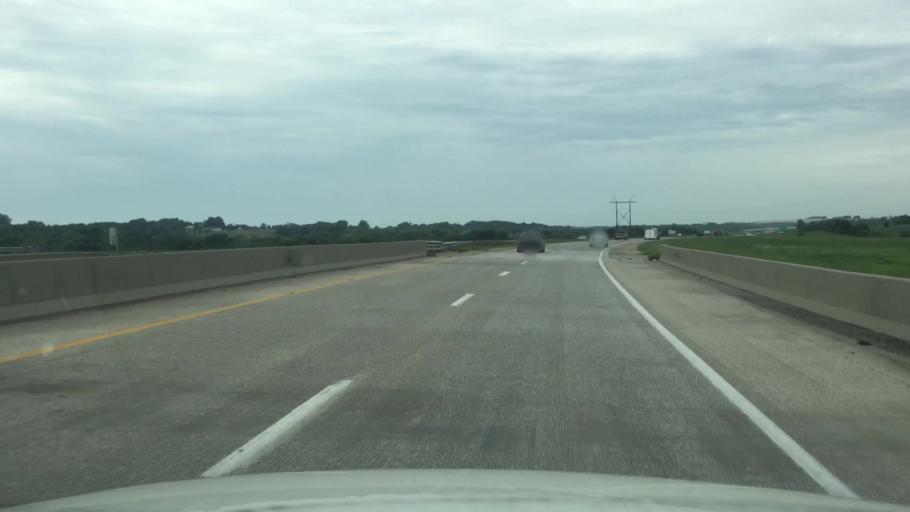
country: US
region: Iowa
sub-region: Warren County
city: Norwalk
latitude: 41.4990
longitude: -93.6259
